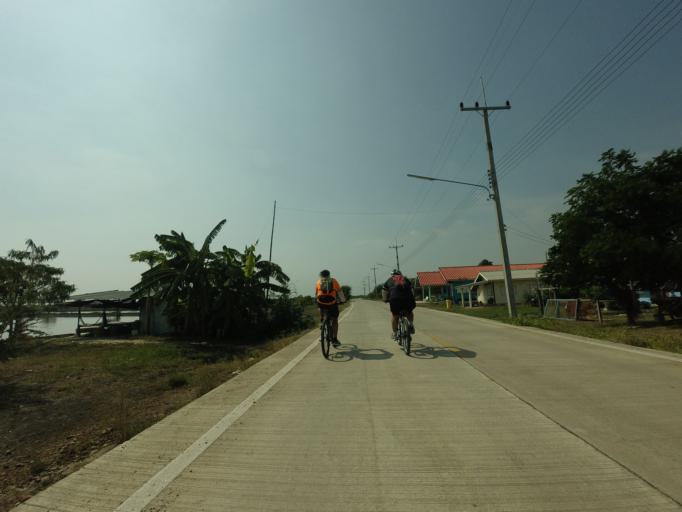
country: TH
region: Samut Sakhon
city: Samut Sakhon
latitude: 13.5134
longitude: 100.3962
